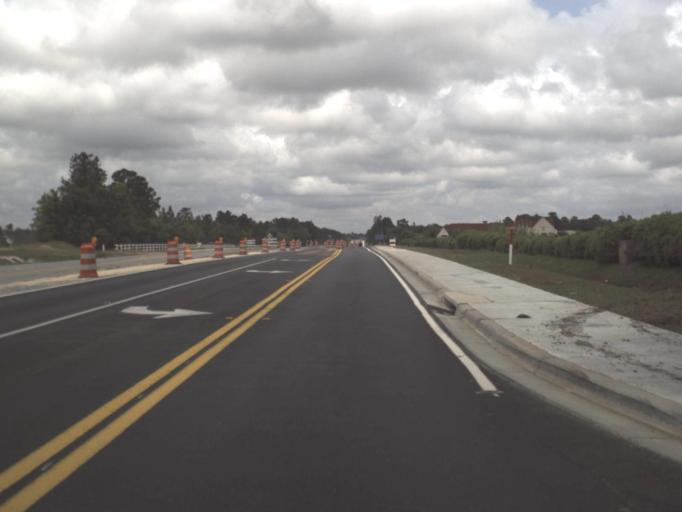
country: US
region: Florida
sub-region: Santa Rosa County
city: Bagdad
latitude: 30.5481
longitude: -87.0870
